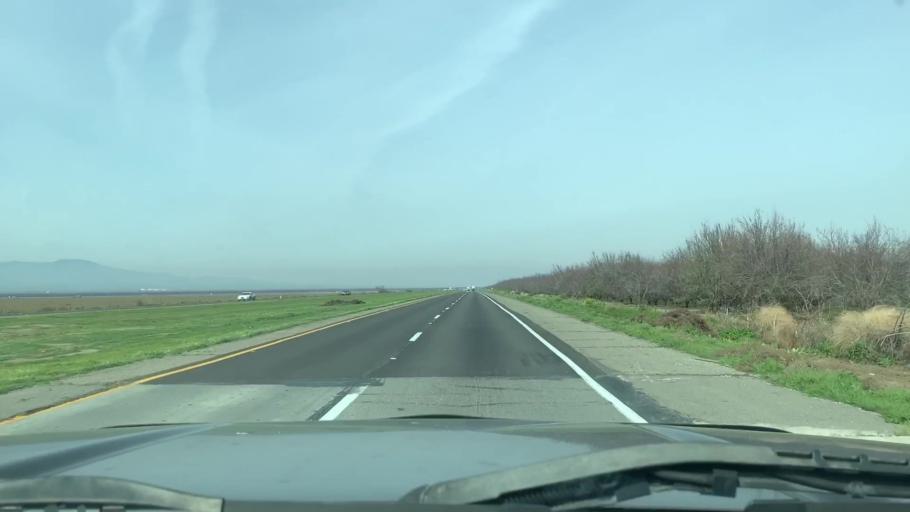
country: US
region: California
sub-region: Fresno County
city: Huron
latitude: 36.1818
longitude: -120.1981
